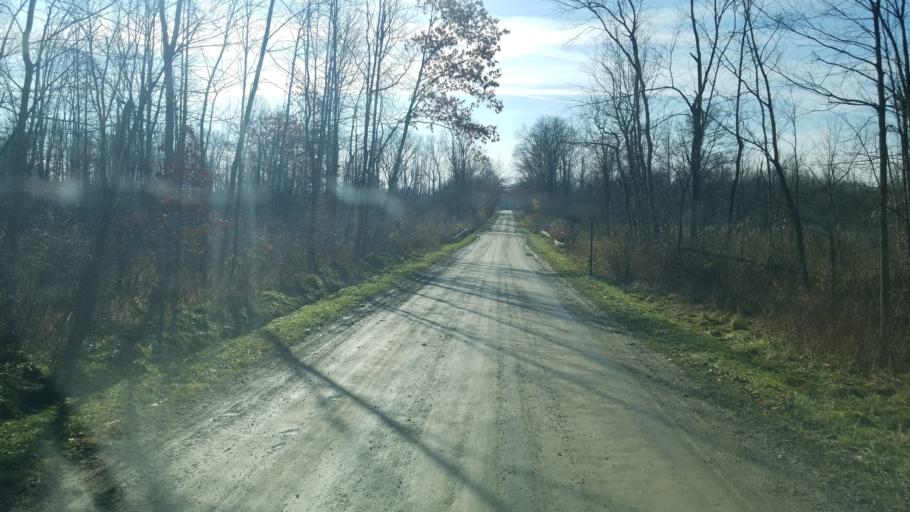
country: US
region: Ohio
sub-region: Ashtabula County
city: Jefferson
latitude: 41.7216
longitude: -80.6848
